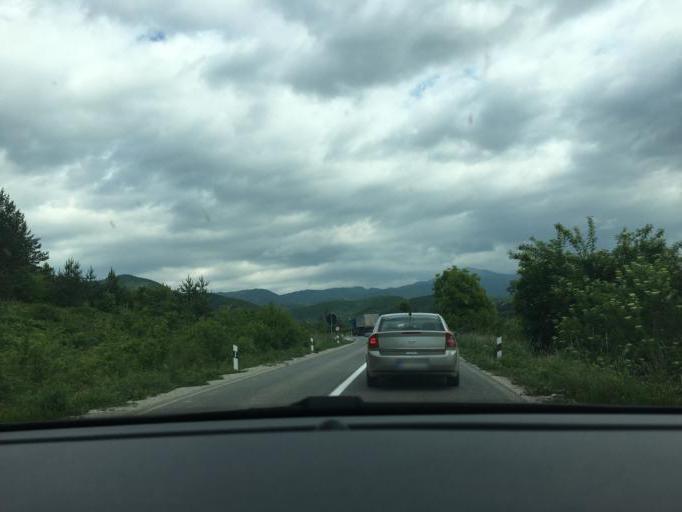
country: MK
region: Resen
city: Jankovec
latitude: 41.1209
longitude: 21.0092
